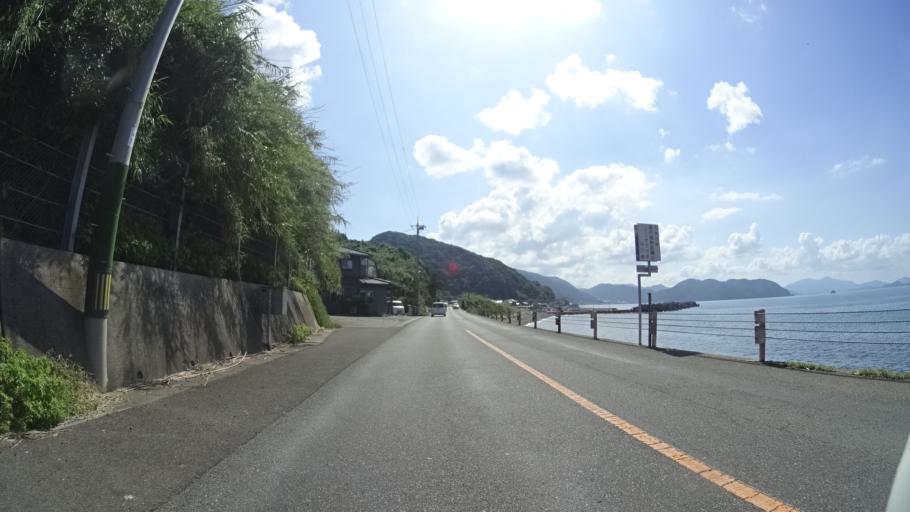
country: JP
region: Yamaguchi
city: Shimonoseki
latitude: 34.2513
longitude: 130.9048
